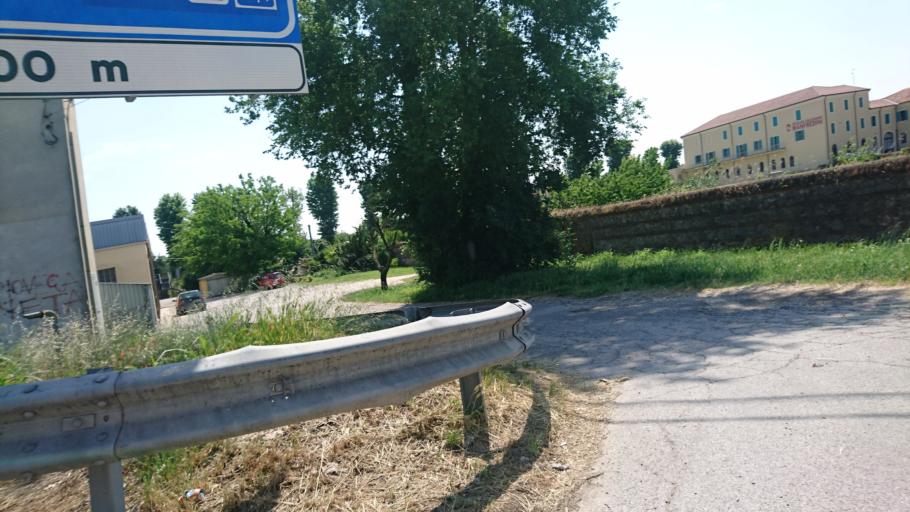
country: IT
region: Veneto
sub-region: Provincia di Padova
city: Ospedaletto Euganeo
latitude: 45.2239
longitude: 11.6305
